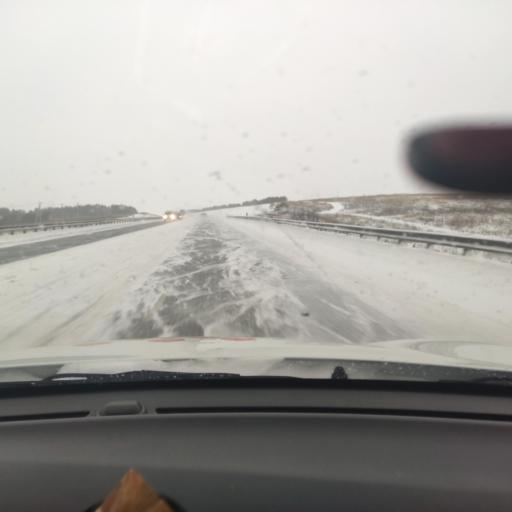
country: RU
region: Tatarstan
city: Verkhniy Uslon
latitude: 55.7179
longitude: 48.8451
